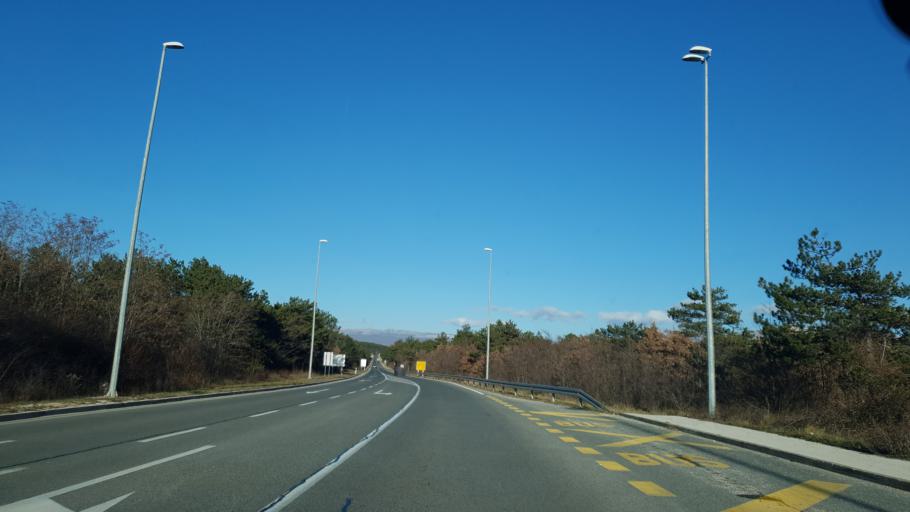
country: HR
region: Splitsko-Dalmatinska
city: Brnaze
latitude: 43.6543
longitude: 16.6395
